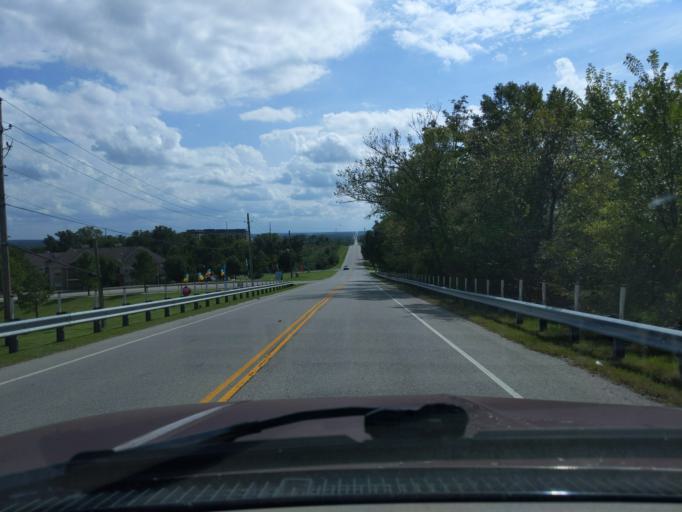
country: US
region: Oklahoma
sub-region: Tulsa County
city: Jenks
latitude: 36.0526
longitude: -96.0116
